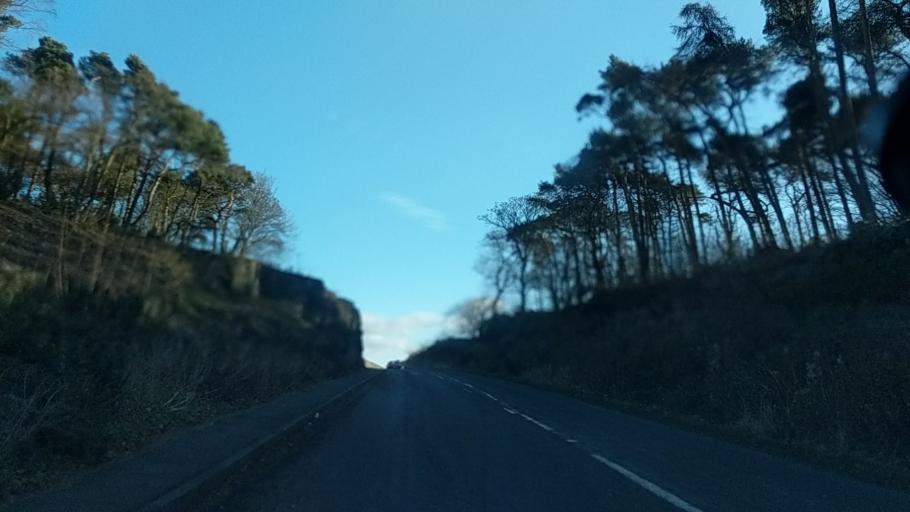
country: GB
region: Scotland
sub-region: Edinburgh
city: Queensferry
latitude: 55.9871
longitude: -3.3666
